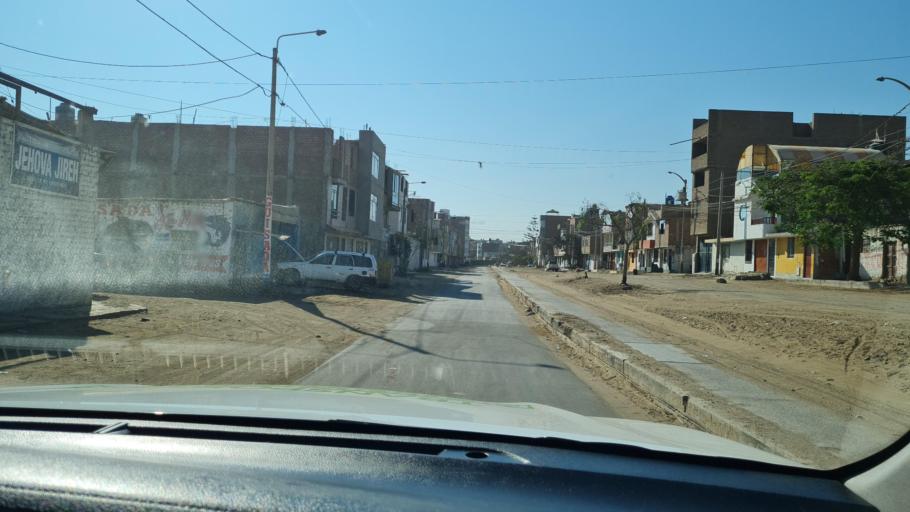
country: PE
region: La Libertad
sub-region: Provincia de Trujillo
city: El Porvenir
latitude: -8.0862
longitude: -79.0118
